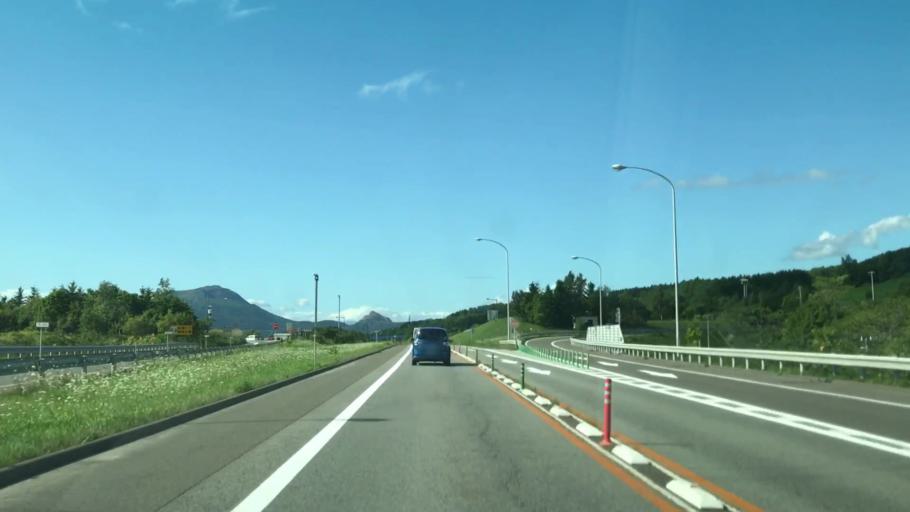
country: JP
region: Hokkaido
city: Date
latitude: 42.4638
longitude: 140.9100
